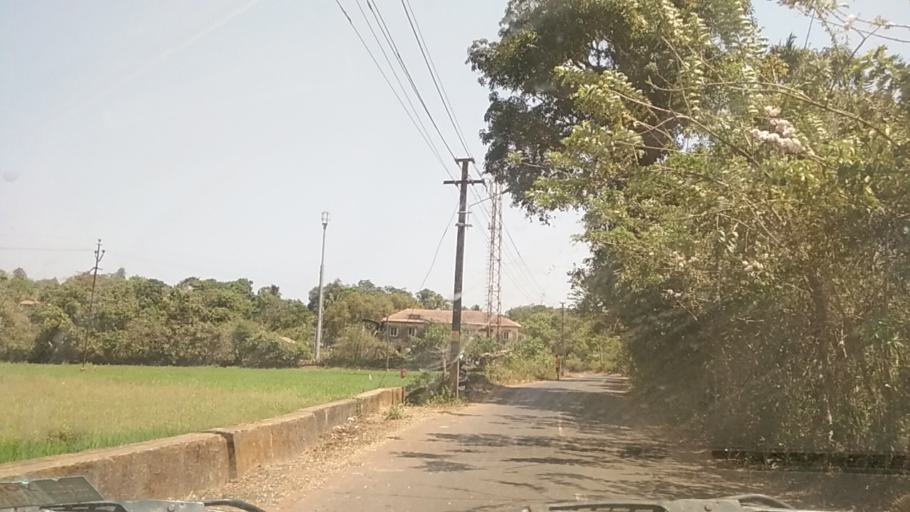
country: IN
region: Goa
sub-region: North Goa
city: Dicholi
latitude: 15.5783
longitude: 73.9196
